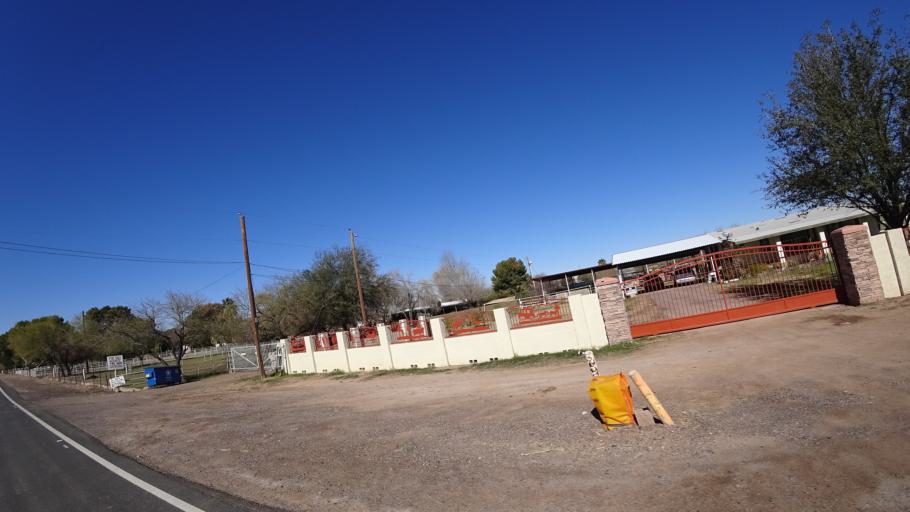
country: US
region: Arizona
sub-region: Maricopa County
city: Tolleson
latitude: 33.3920
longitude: -112.2909
